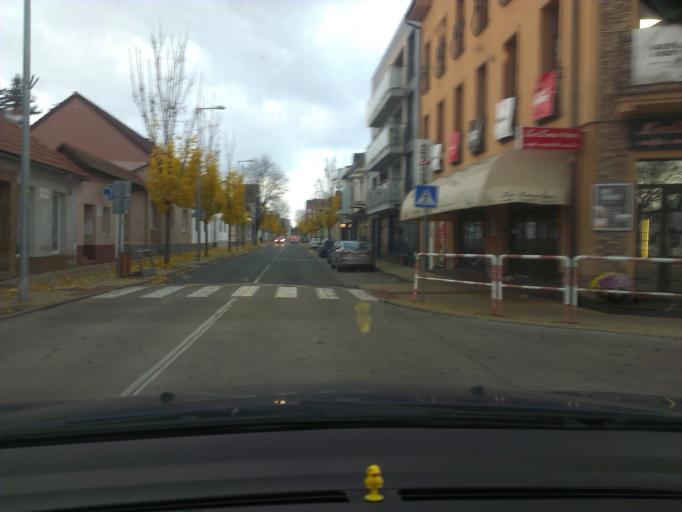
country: SK
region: Trnavsky
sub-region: Okres Trnava
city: Piestany
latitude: 48.5913
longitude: 17.8283
